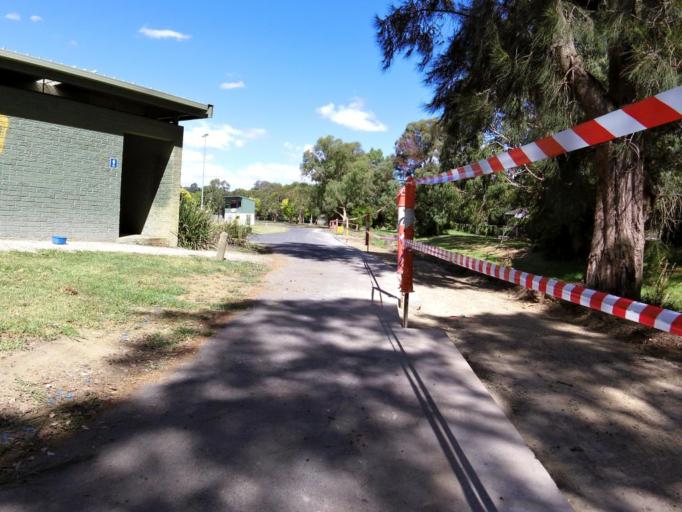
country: AU
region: Victoria
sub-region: Yarra Ranges
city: Kilsyth
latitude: -37.7931
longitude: 145.3245
